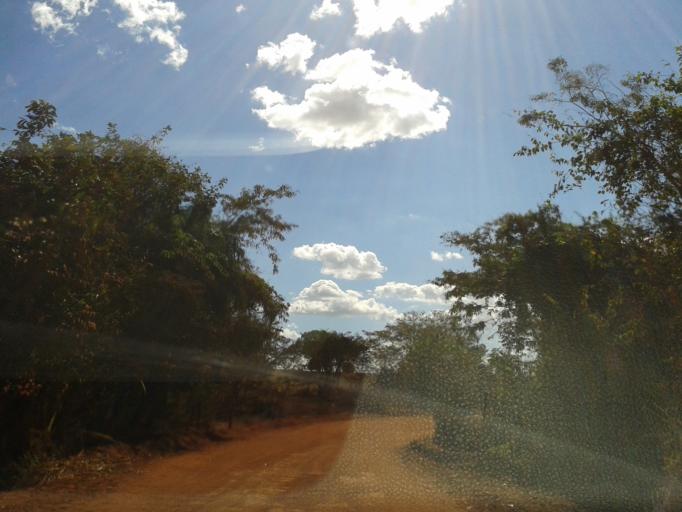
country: BR
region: Minas Gerais
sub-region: Capinopolis
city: Capinopolis
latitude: -18.6108
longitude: -49.4950
